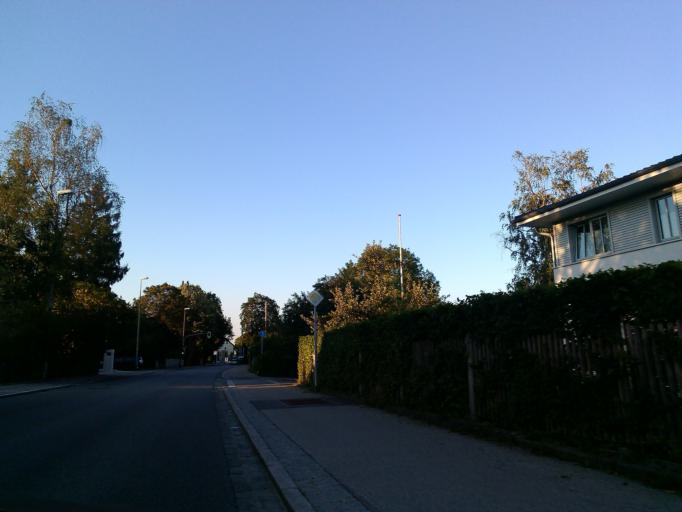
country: DE
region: Bavaria
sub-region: Upper Bavaria
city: Krailling
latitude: 48.0856
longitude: 11.4022
